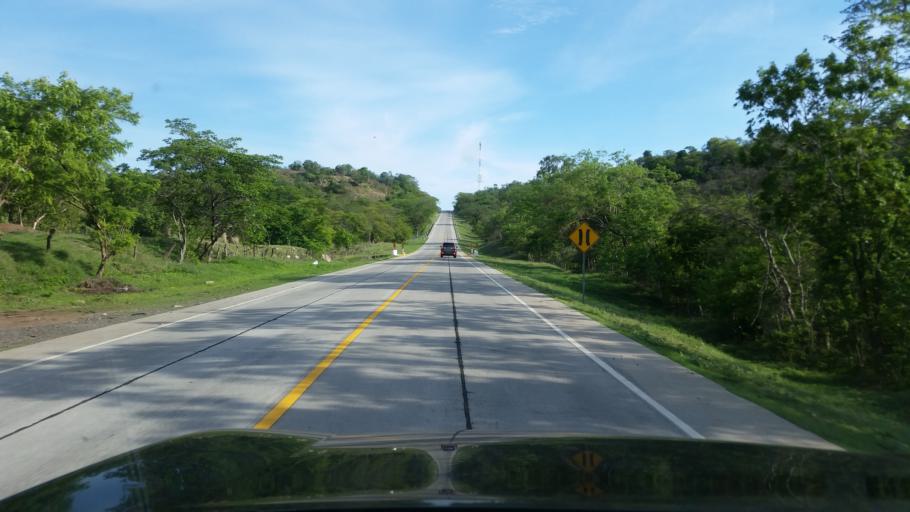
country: NI
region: Leon
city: Nagarote
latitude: 12.1651
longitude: -86.6610
